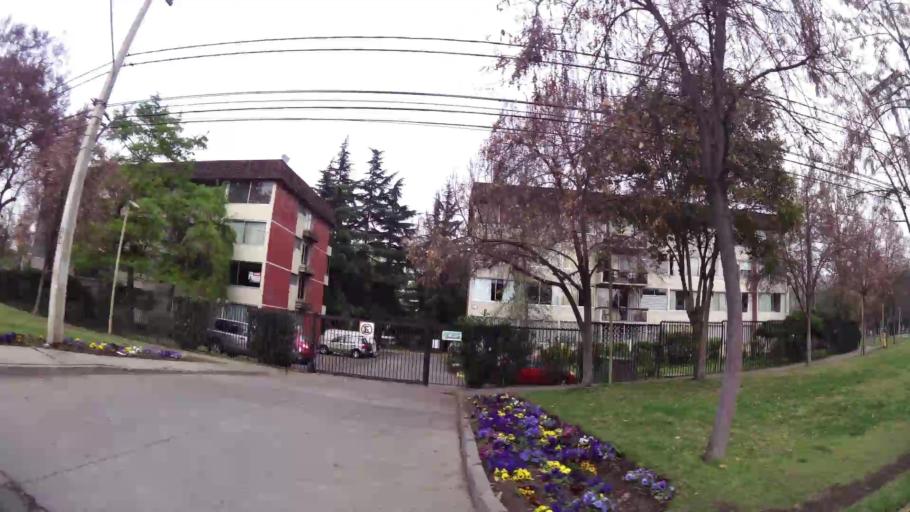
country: CL
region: Santiago Metropolitan
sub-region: Provincia de Santiago
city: Villa Presidente Frei, Nunoa, Santiago, Chile
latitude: -33.4099
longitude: -70.5421
